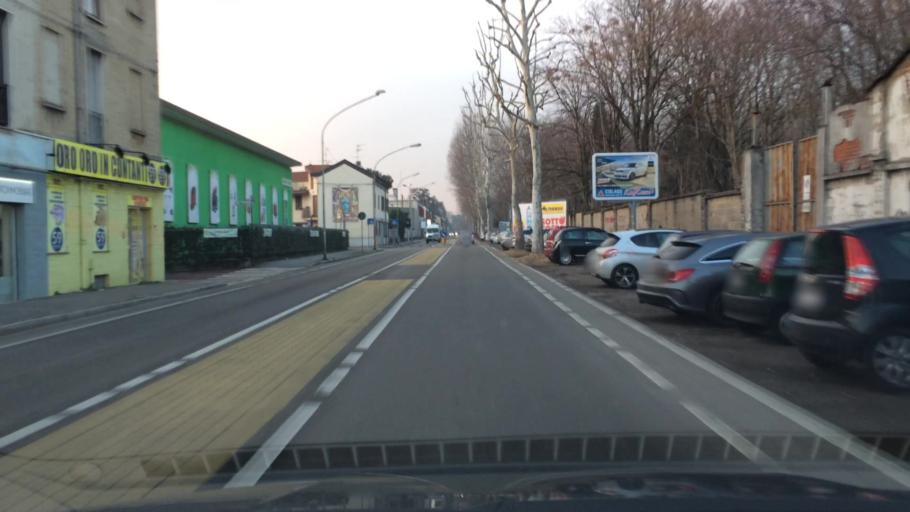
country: IT
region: Lombardy
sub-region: Provincia di Varese
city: Saronno
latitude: 45.6190
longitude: 9.0303
